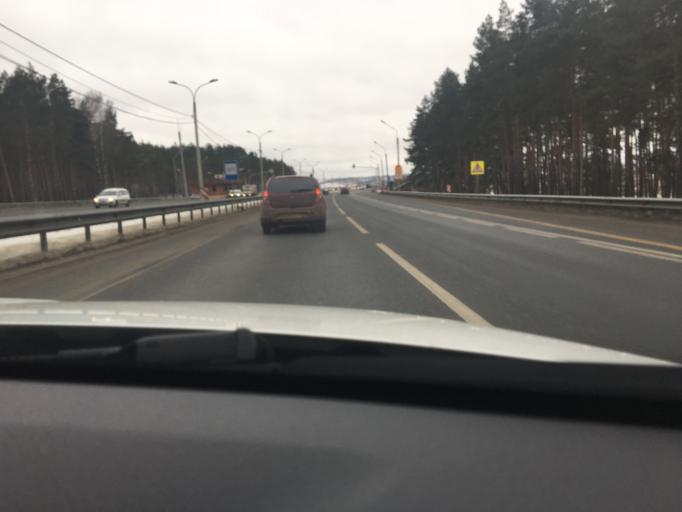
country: RU
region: Moskovskaya
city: Danki
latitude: 54.8842
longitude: 37.5112
